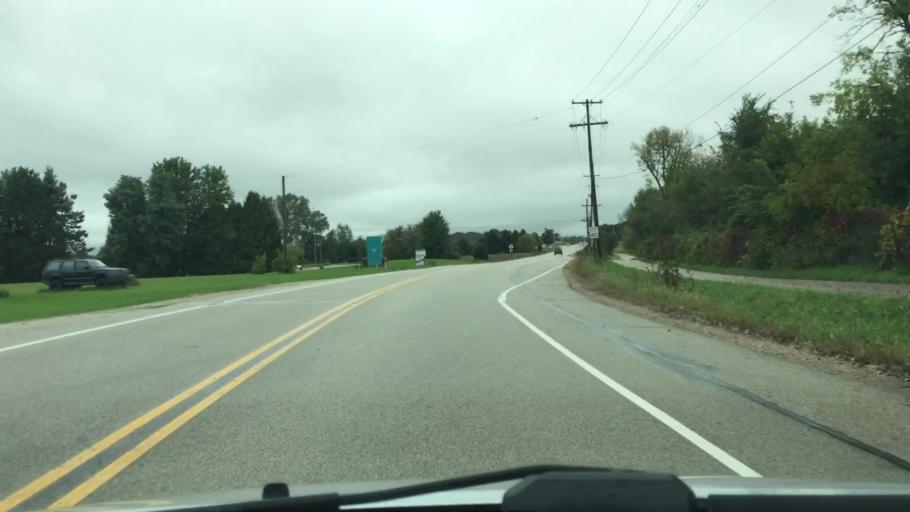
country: US
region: Wisconsin
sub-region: Waukesha County
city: Dousman
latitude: 43.0165
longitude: -88.4624
